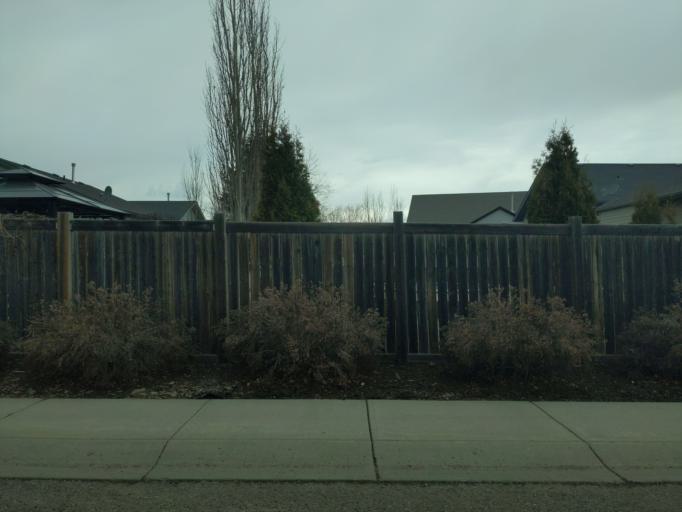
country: CA
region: Saskatchewan
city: Lloydminster
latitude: 53.2569
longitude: -110.0365
